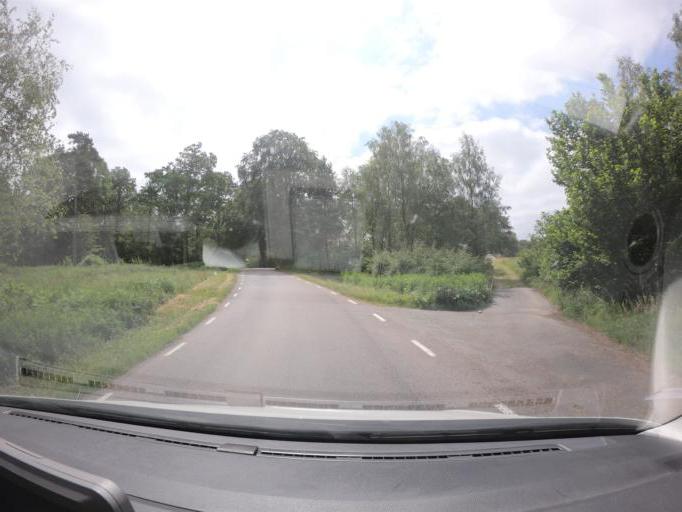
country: SE
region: Skane
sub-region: Hassleholms Kommun
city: Sosdala
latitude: 56.0586
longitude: 13.6015
